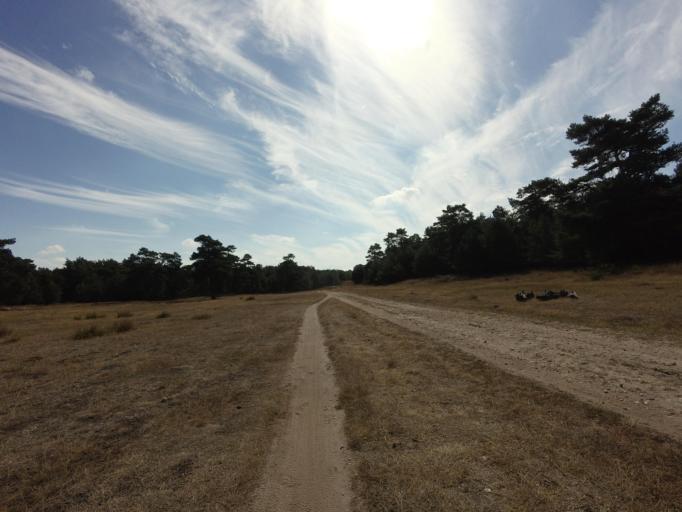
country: NL
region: Gelderland
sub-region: Gemeente Rheden
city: Rheden
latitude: 52.0432
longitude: 6.0054
